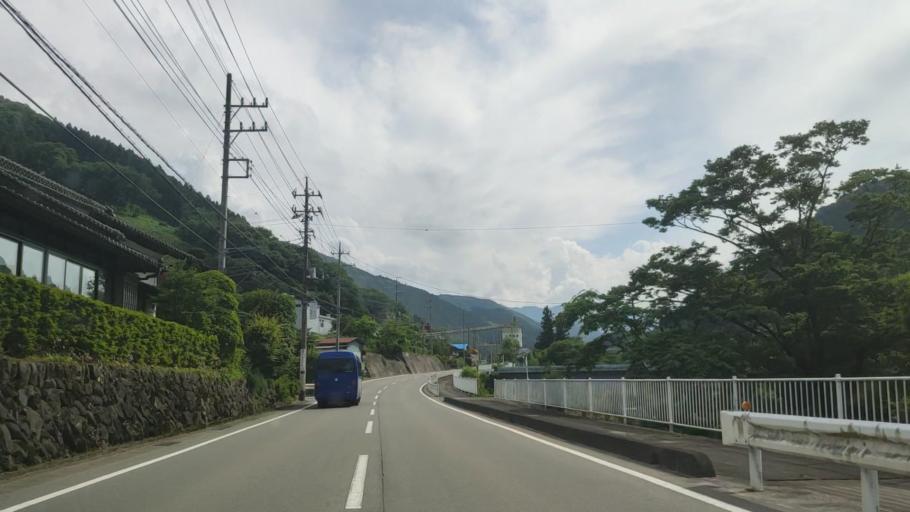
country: JP
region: Gunma
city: Tomioka
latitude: 36.1894
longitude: 138.7506
